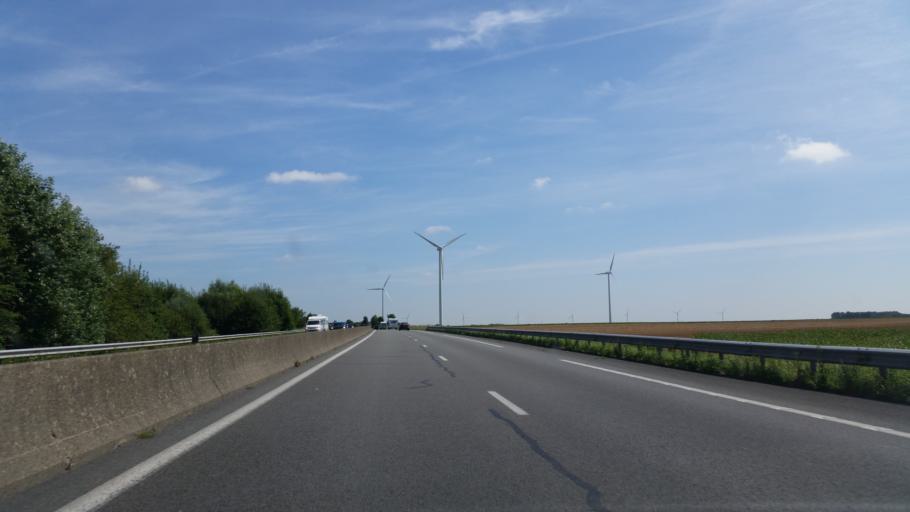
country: FR
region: Picardie
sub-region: Departement de la Somme
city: Rosieres-en-Santerre
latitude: 49.8532
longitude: 2.7381
